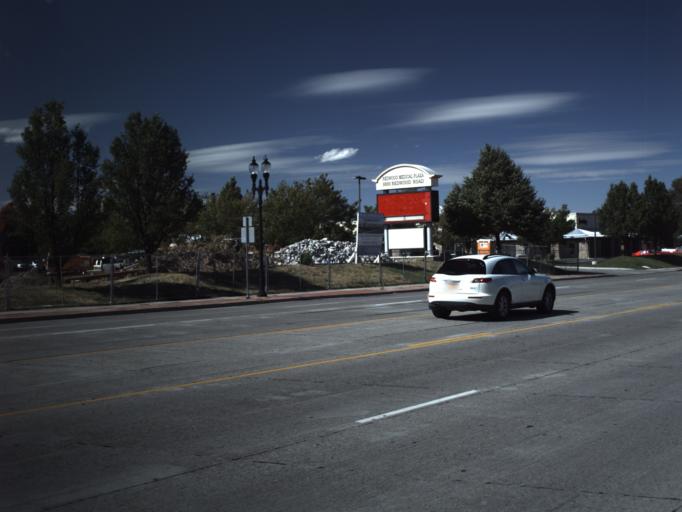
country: US
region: Utah
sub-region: Salt Lake County
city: West Jordan
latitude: 40.5902
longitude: -111.9386
